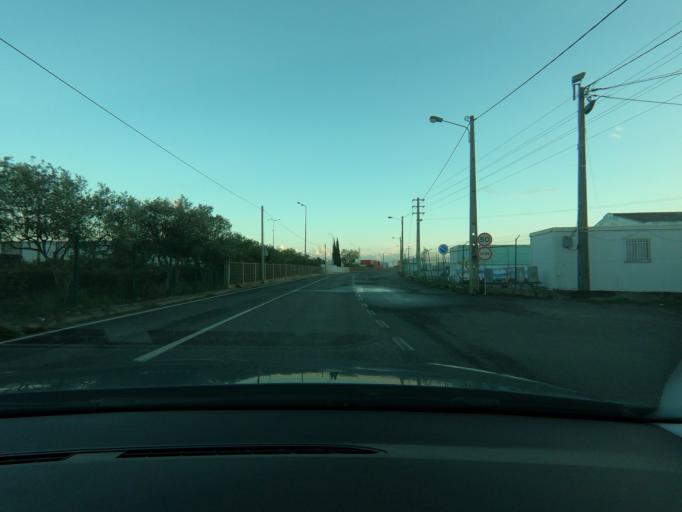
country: PT
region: Lisbon
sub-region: Vila Franca de Xira
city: Castanheira do Ribatejo
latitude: 38.9954
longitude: -8.9631
